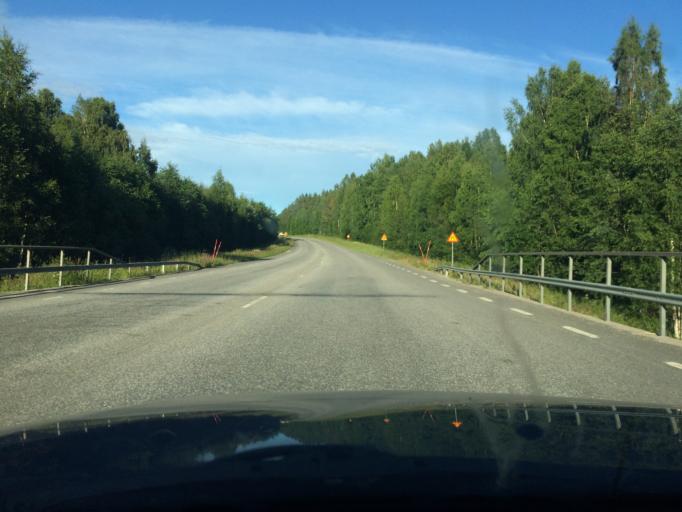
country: SE
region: Norrbotten
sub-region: Pitea Kommun
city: Roknas
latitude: 65.3180
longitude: 21.2511
